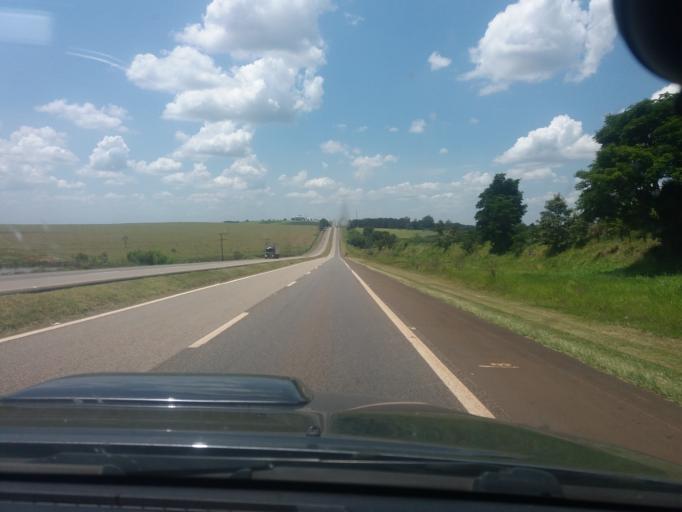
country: BR
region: Sao Paulo
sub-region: Itapetininga
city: Itapetininga
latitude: -23.5091
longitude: -47.9686
